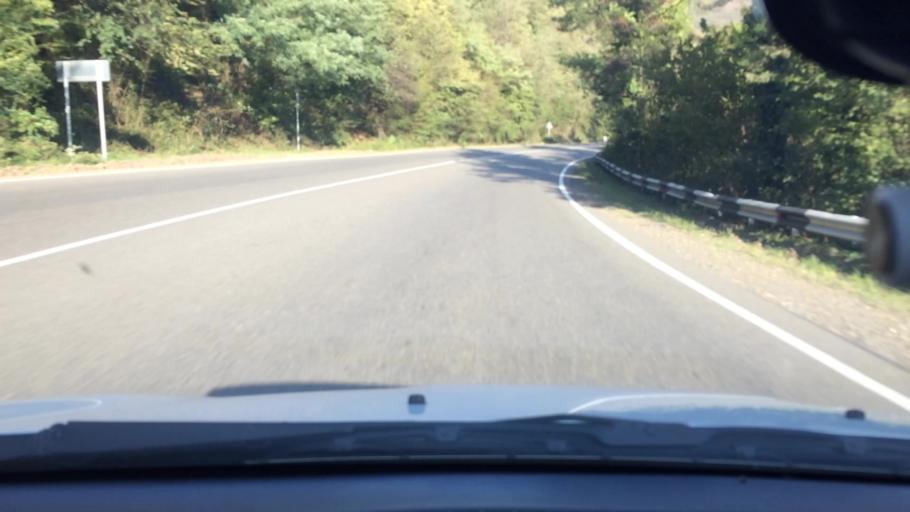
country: GE
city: Shorapani
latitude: 42.0922
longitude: 43.1301
